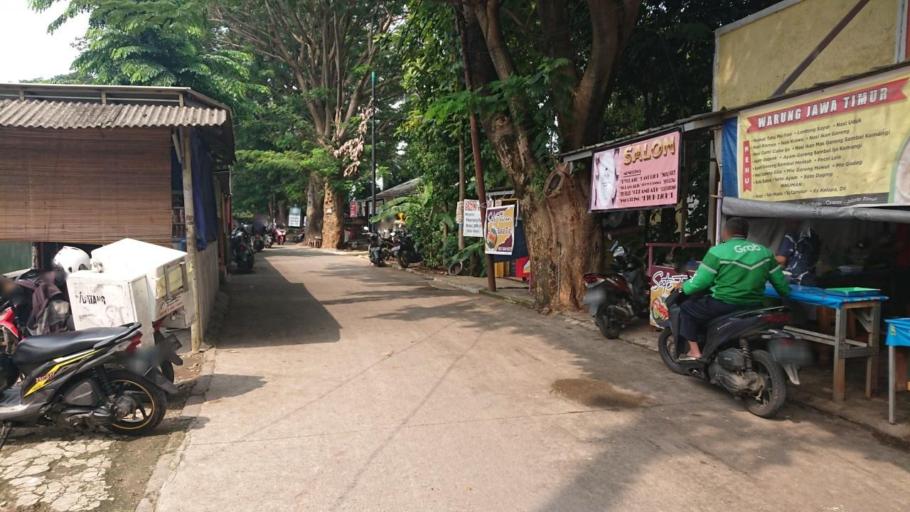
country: ID
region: West Java
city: Depok
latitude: -6.3360
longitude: 106.8850
